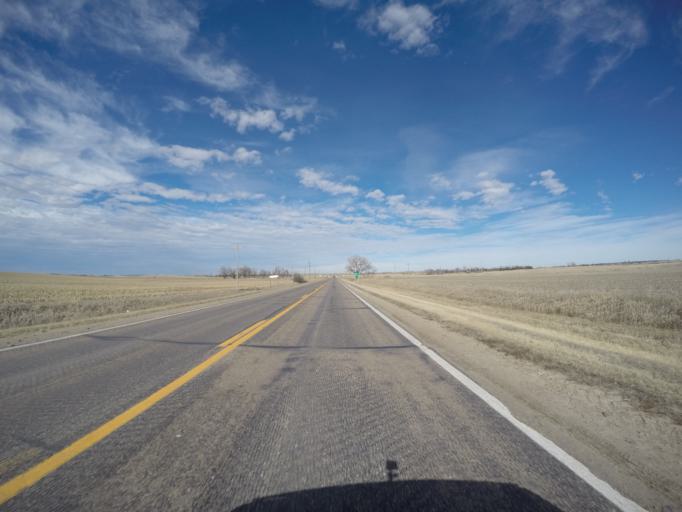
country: US
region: Nebraska
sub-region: Franklin County
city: Franklin
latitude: 40.2901
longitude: -98.9526
